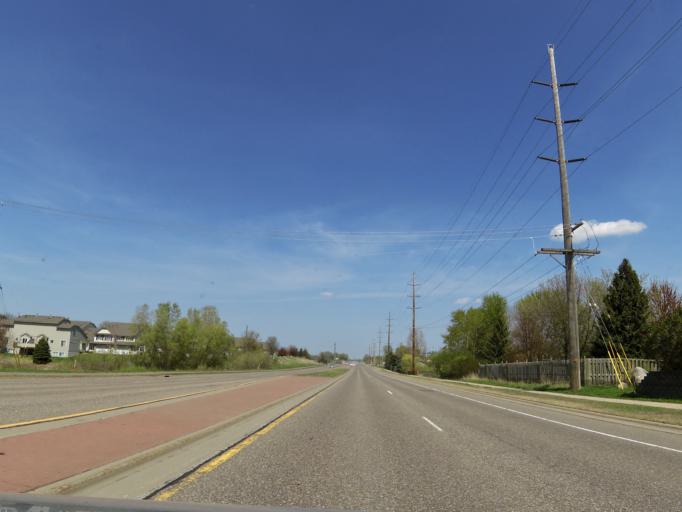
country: US
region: Minnesota
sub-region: Scott County
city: Savage
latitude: 44.7508
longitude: -93.3591
